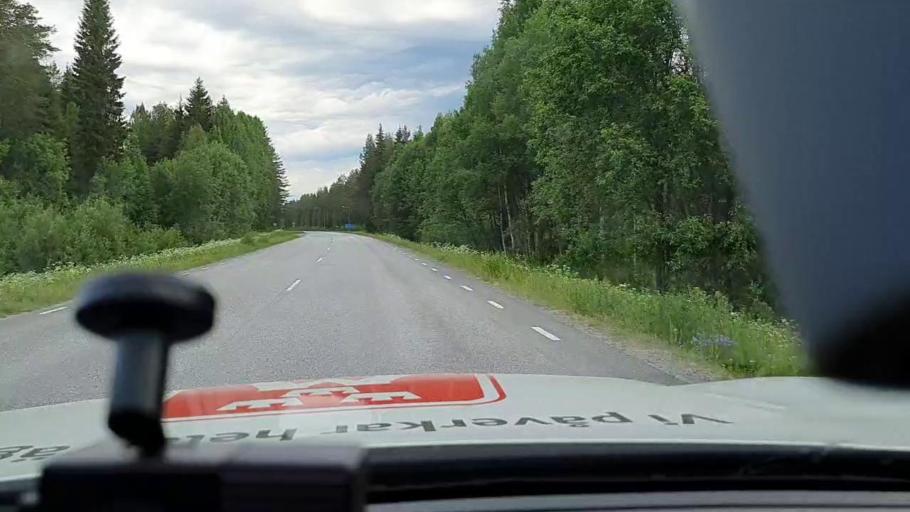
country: SE
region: Norrbotten
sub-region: Bodens Kommun
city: Boden
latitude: 65.8056
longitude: 21.6564
